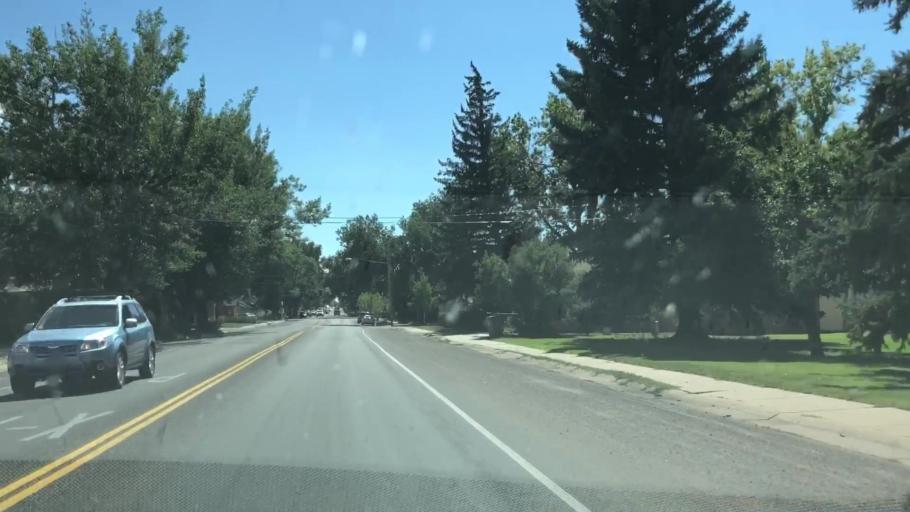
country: US
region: Wyoming
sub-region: Albany County
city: Laramie
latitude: 41.3208
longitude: -105.5847
